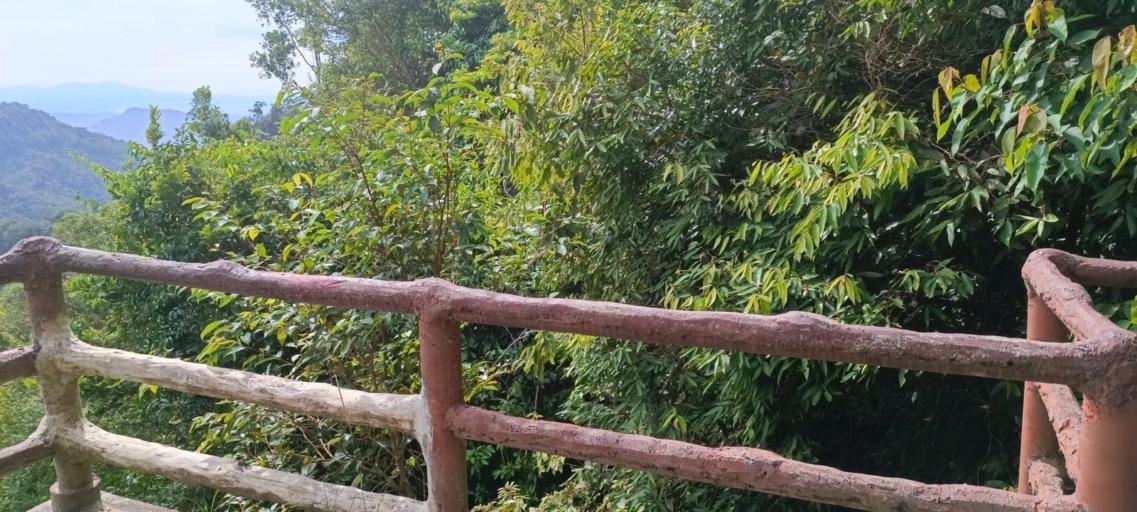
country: MY
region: Penang
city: Bukit Mertajam
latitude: 5.3696
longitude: 100.4847
